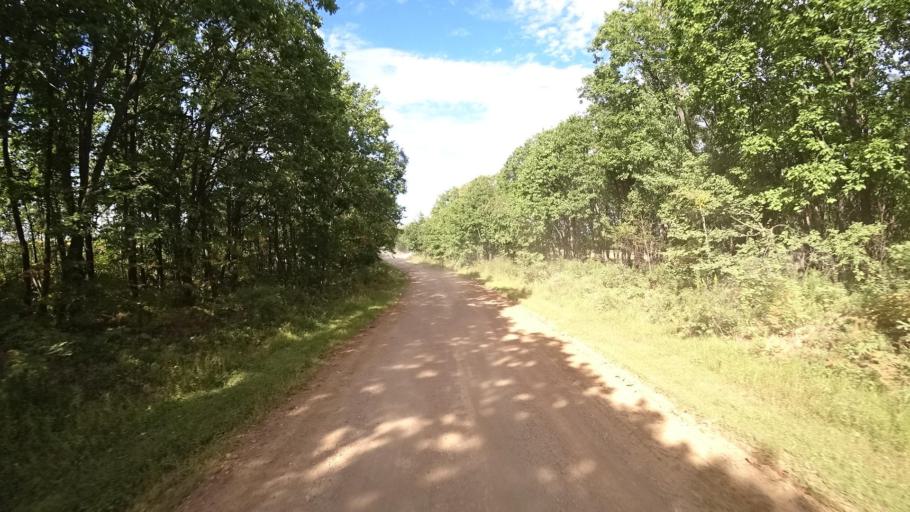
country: RU
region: Primorskiy
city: Yakovlevka
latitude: 44.4145
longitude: 133.5703
